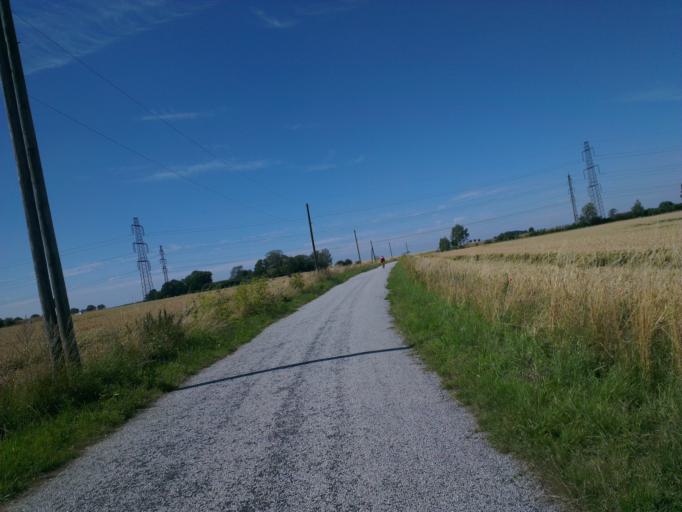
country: DK
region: Capital Region
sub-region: Frederikssund Kommune
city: Slangerup
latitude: 55.8532
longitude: 12.1633
